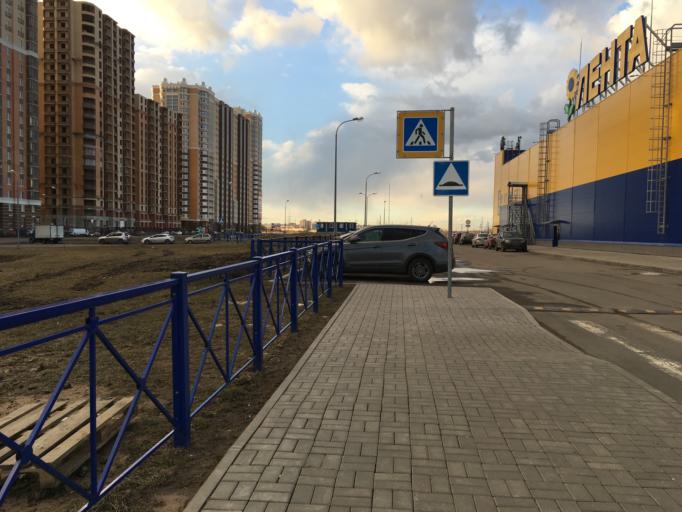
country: RU
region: St.-Petersburg
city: Krasnogvargeisky
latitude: 59.9166
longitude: 30.5209
